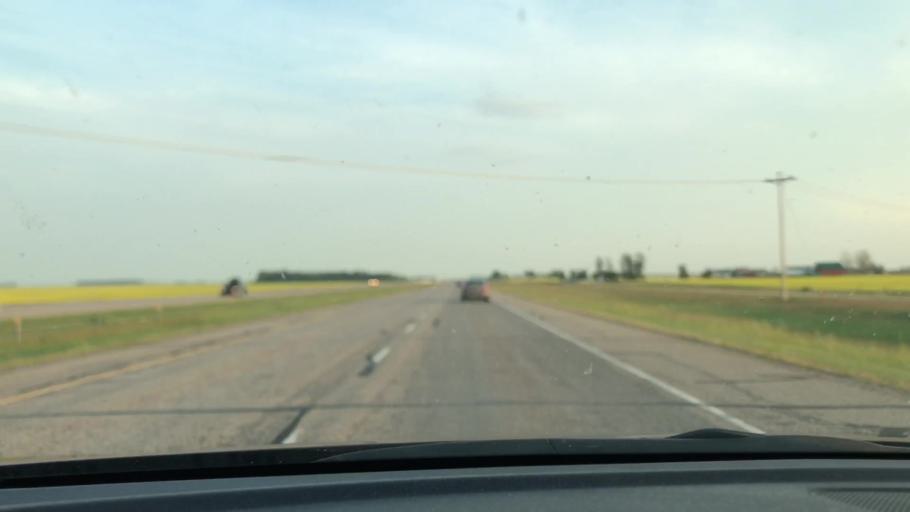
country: CA
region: Alberta
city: Olds
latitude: 51.8462
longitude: -114.0256
